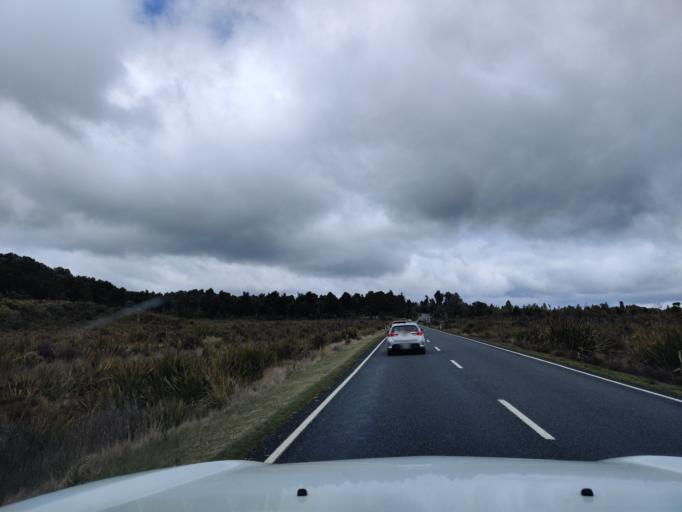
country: NZ
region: Manawatu-Wanganui
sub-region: Ruapehu District
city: Waiouru
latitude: -39.2299
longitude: 175.3948
